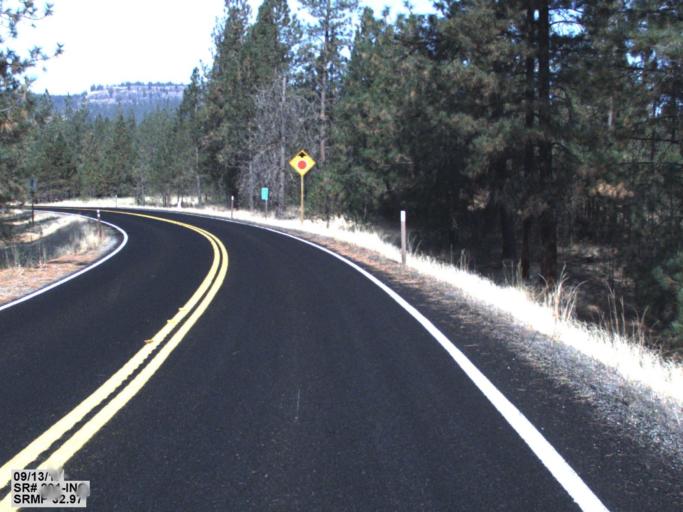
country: US
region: Washington
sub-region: Spokane County
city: Fairchild Air Force Base
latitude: 47.8479
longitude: -117.8528
